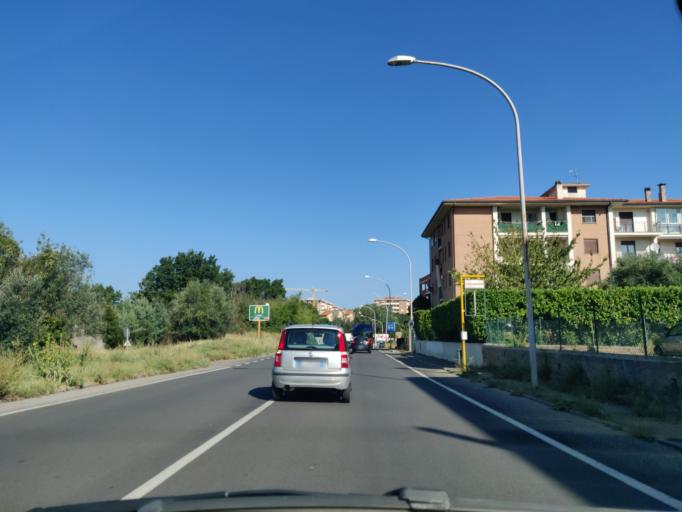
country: IT
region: Latium
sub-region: Provincia di Viterbo
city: Viterbo
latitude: 42.4221
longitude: 12.0941
